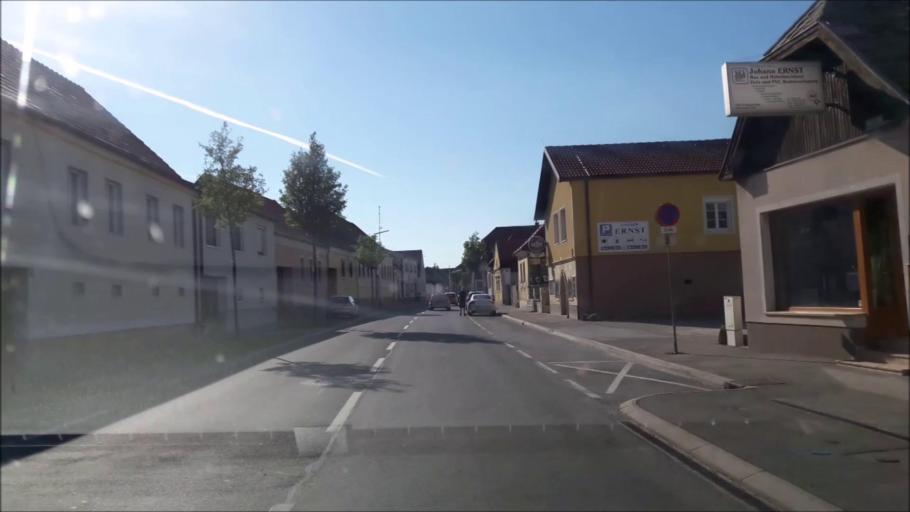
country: AT
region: Burgenland
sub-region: Eisenstadt-Umgebung
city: Sankt Margarethen im Burgenland
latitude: 47.8043
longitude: 16.6100
